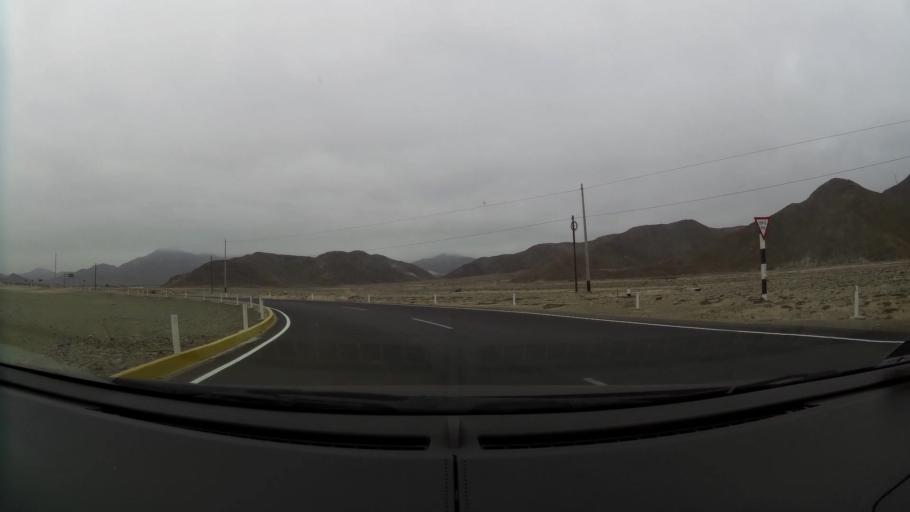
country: PE
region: La Libertad
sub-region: Viru
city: Chao
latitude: -8.6481
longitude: -78.6212
